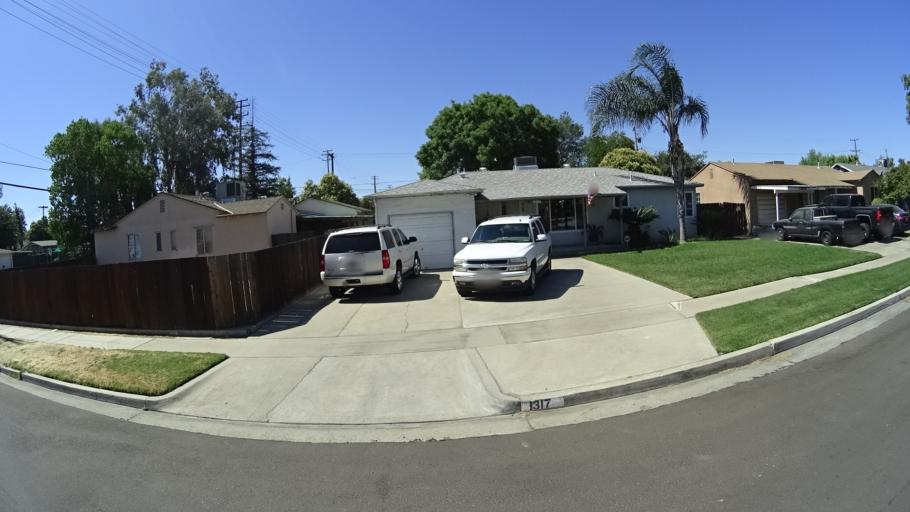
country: US
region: California
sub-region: Fresno County
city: Fresno
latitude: 36.7846
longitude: -119.8269
